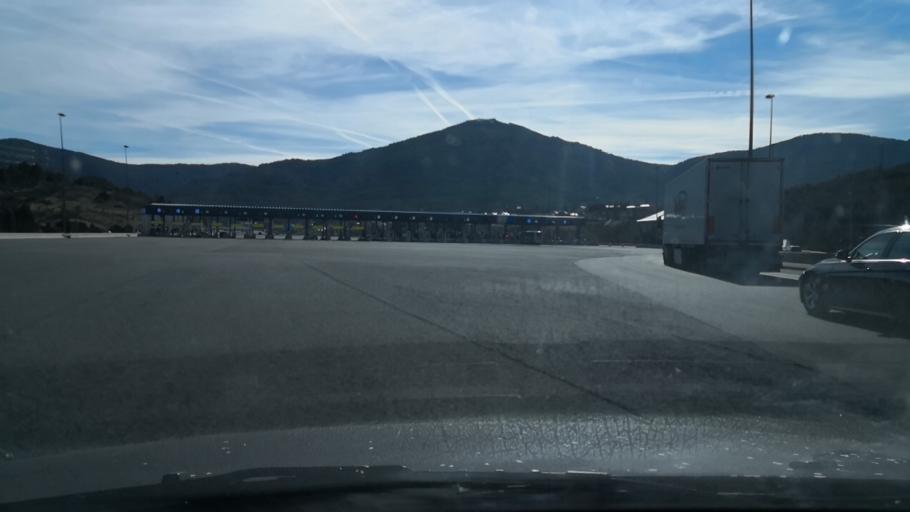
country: ES
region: Castille and Leon
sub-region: Provincia de Segovia
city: Otero de Herreros
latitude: 40.7276
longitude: -4.1936
